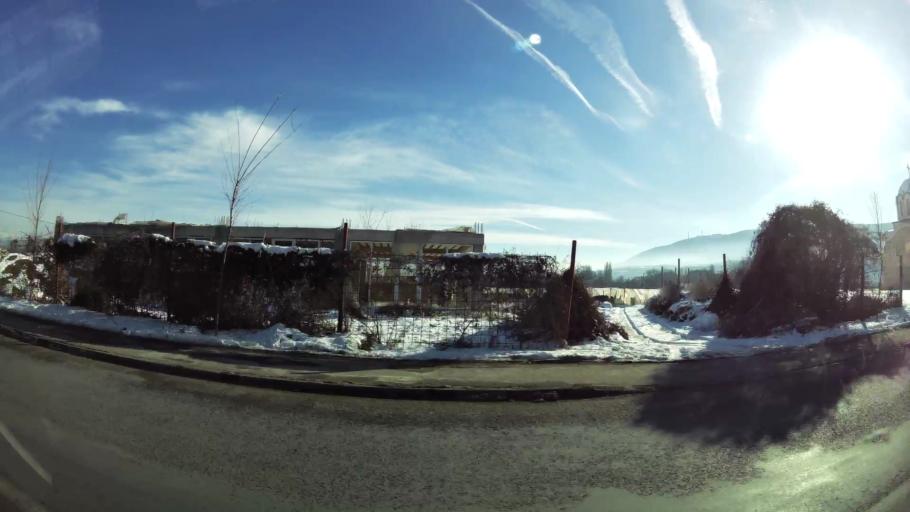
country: MK
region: Saraj
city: Saraj
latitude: 42.0048
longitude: 21.3326
